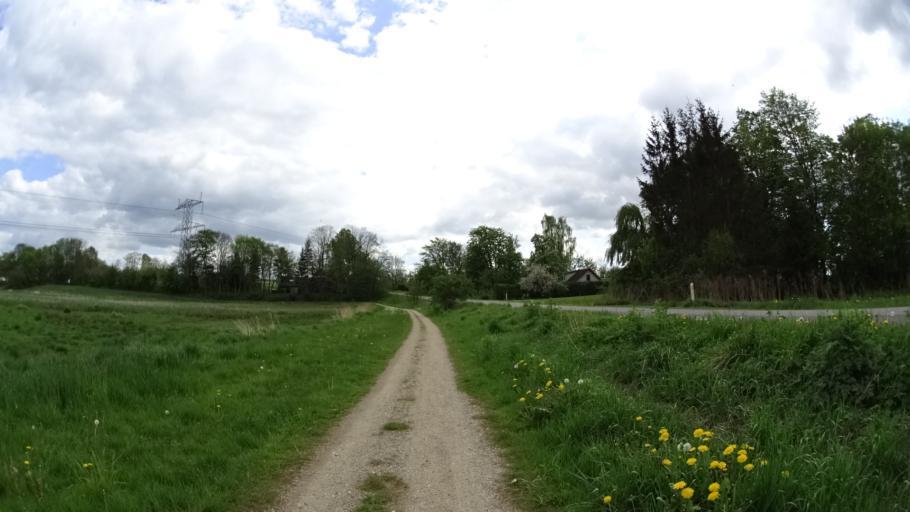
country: DK
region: Central Jutland
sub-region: Arhus Kommune
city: Framlev
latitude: 56.1321
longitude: 10.0406
